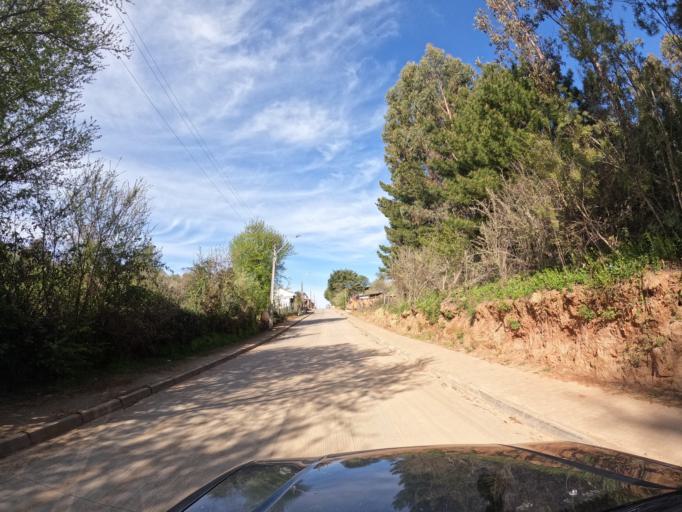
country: CL
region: Biobio
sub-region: Provincia de Biobio
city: La Laja
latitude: -37.1308
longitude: -72.7315
